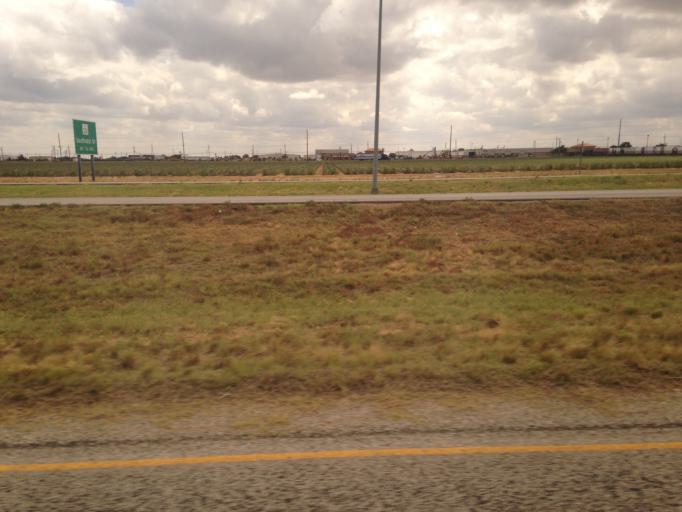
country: US
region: Texas
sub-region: Lubbock County
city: Lubbock
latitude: 33.5319
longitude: -101.8112
